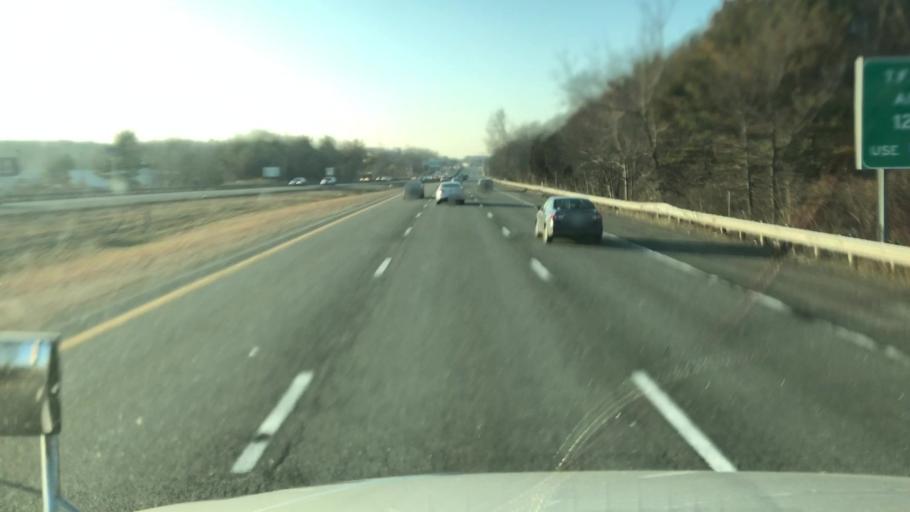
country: US
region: Massachusetts
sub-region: Bristol County
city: Seekonk
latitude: 41.8043
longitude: -71.3345
